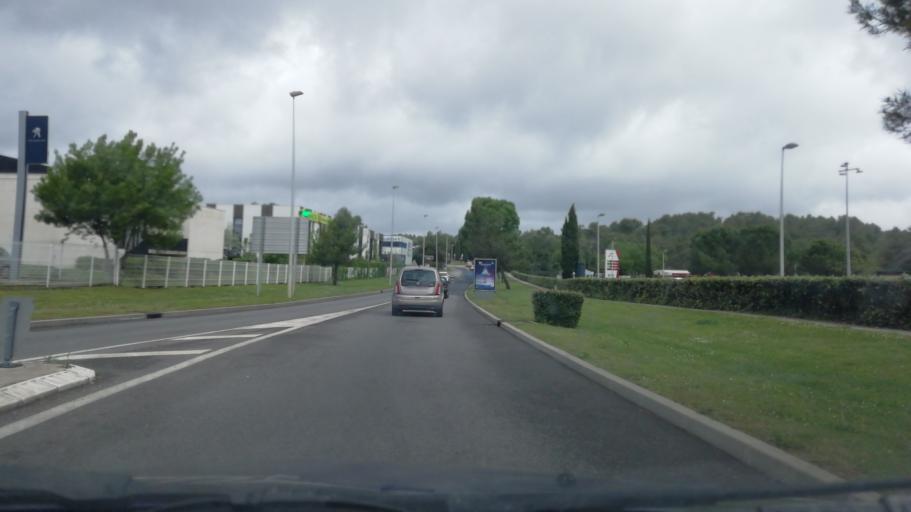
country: FR
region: Languedoc-Roussillon
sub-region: Departement de l'Herault
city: Saint-Clement-de-Riviere
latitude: 43.6764
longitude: 3.8177
